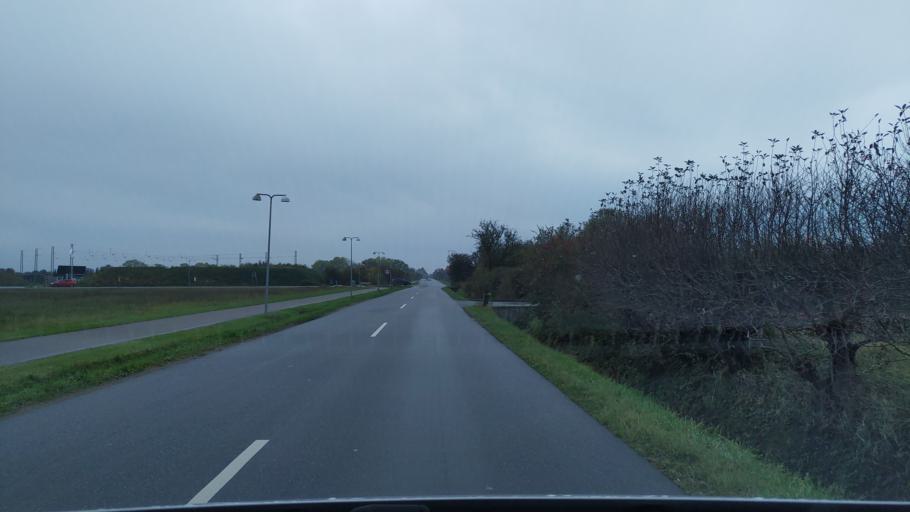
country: DK
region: Capital Region
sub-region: Dragor Kommune
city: Dragor
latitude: 55.5847
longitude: 12.6262
